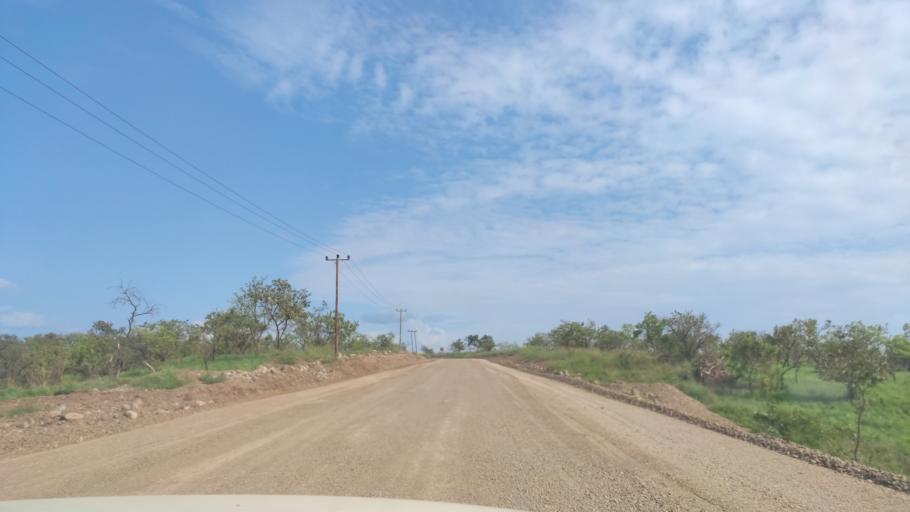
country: ET
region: Southern Nations, Nationalities, and People's Region
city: Felege Neway
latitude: 6.4254
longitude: 37.2189
